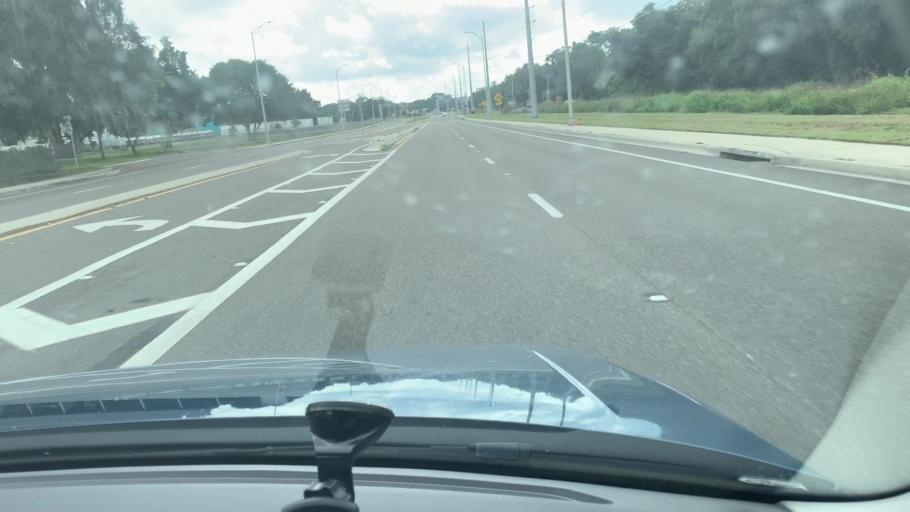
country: US
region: Florida
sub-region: Polk County
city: Kathleen
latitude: 28.1034
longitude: -82.0118
